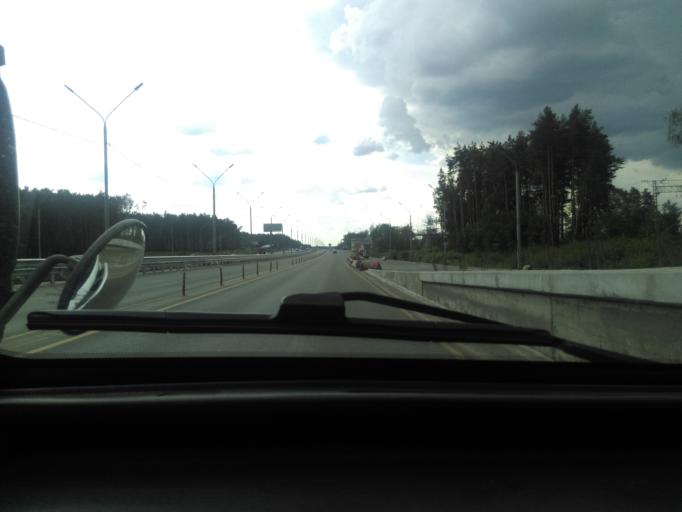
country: RU
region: Moskovskaya
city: Yakovlevskoye
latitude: 55.4331
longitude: 37.8775
